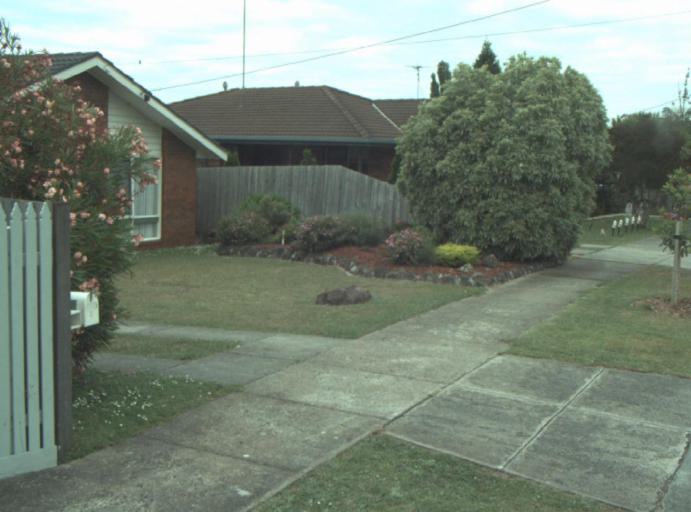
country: AU
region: Victoria
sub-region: Greater Geelong
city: Wandana Heights
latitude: -38.1996
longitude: 144.3311
